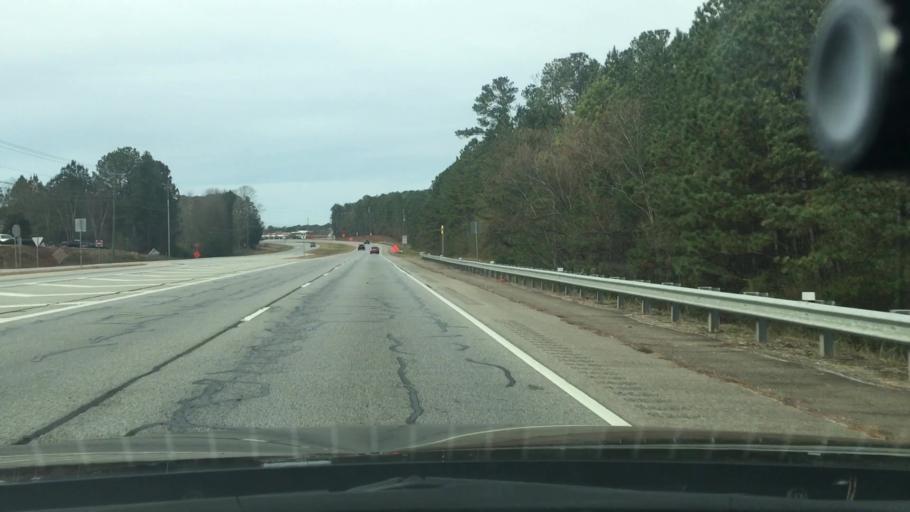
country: US
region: Georgia
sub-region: Fayette County
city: Peachtree City
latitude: 33.4034
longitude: -84.6639
